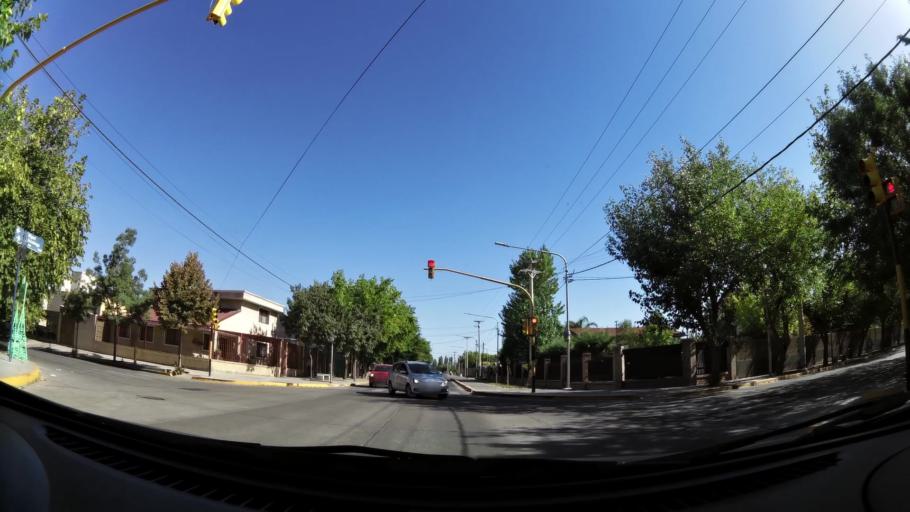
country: AR
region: Mendoza
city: Villa Nueva
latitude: -32.9153
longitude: -68.7985
